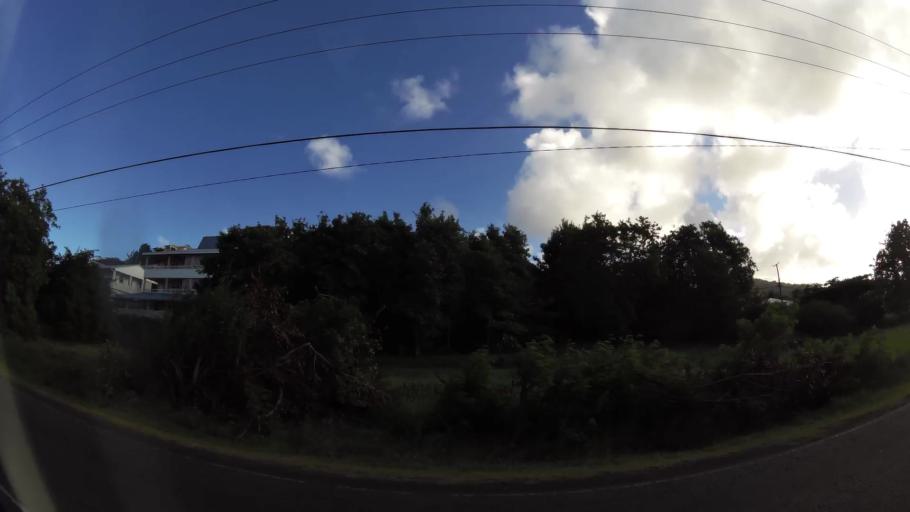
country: LC
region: Gros-Islet
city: Gros Islet
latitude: 14.0685
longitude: -60.9510
